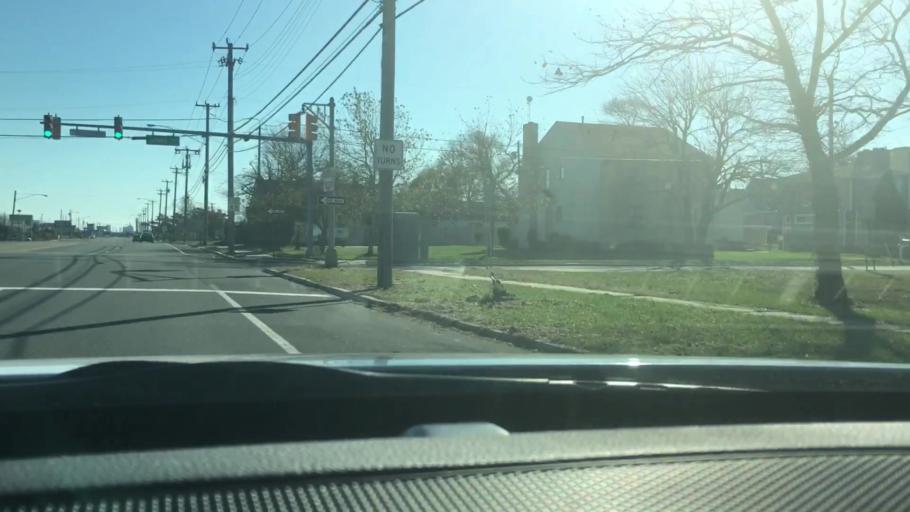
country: US
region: New Jersey
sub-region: Atlantic County
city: Pleasantville
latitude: 39.3858
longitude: -74.5089
